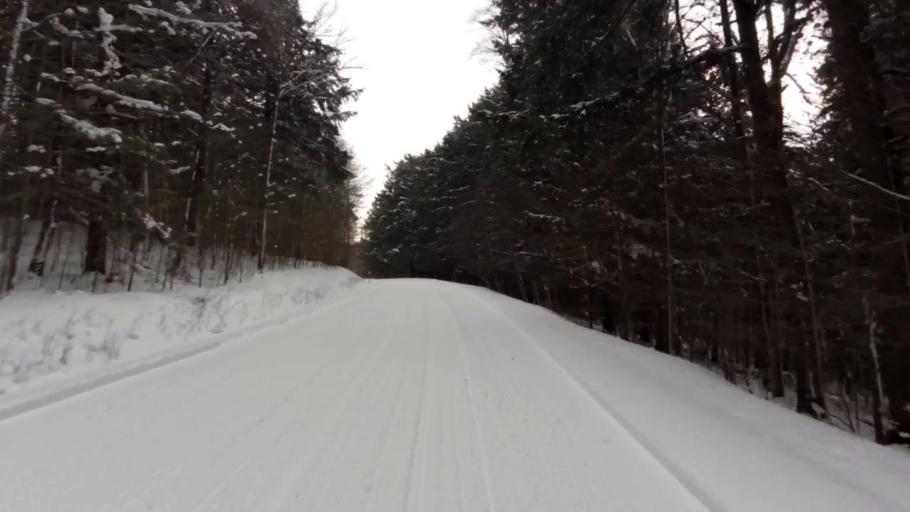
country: US
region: New York
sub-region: Cattaraugus County
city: Salamanca
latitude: 42.0594
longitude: -78.7630
